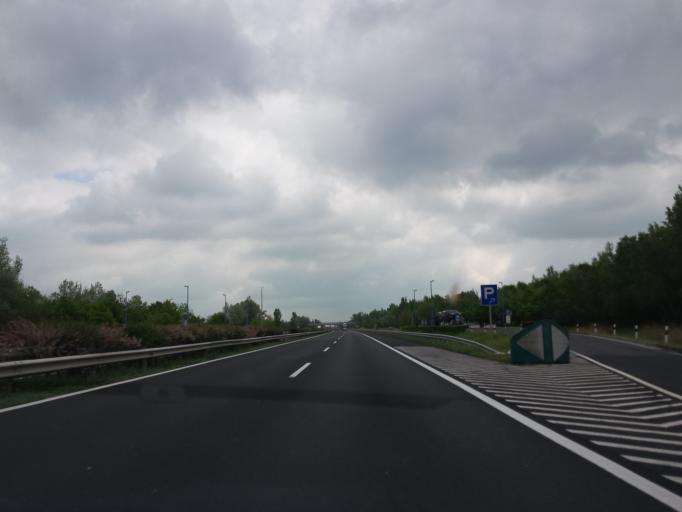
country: HU
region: Gyor-Moson-Sopron
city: Kimle
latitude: 47.7906
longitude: 17.3259
